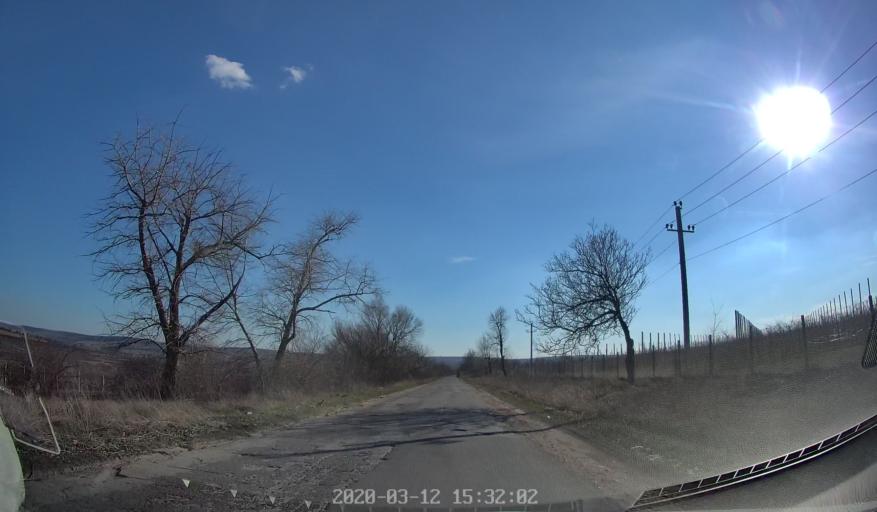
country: MD
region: Chisinau
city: Ciorescu
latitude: 47.1548
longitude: 28.9419
